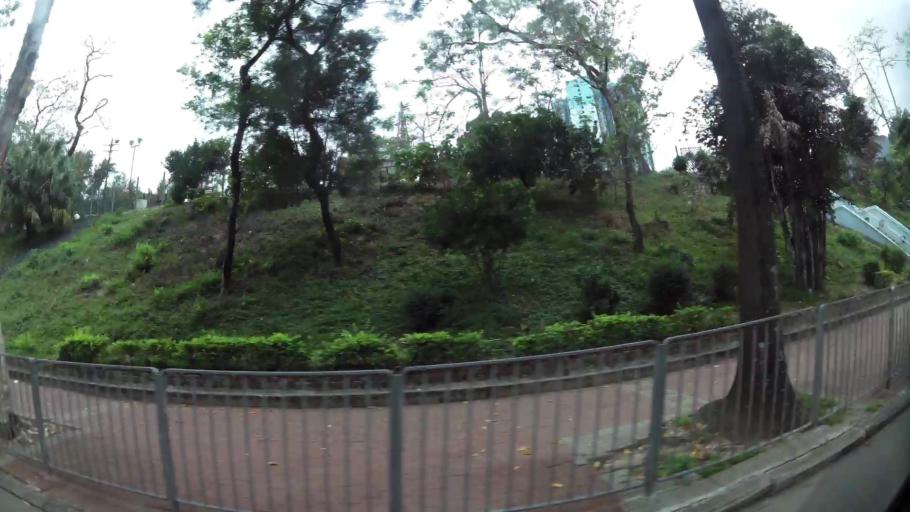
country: HK
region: Wong Tai Sin
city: Wong Tai Sin
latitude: 22.3357
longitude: 114.1914
